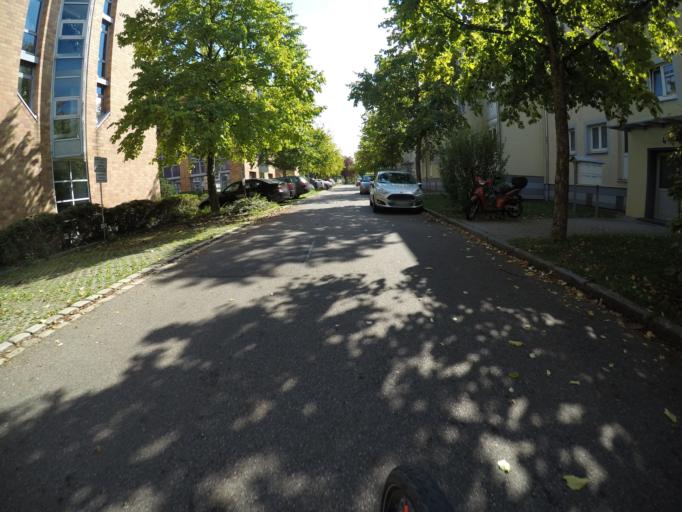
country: DE
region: Baden-Wuerttemberg
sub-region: Regierungsbezirk Stuttgart
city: Steinenbronn
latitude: 48.7268
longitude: 9.1097
